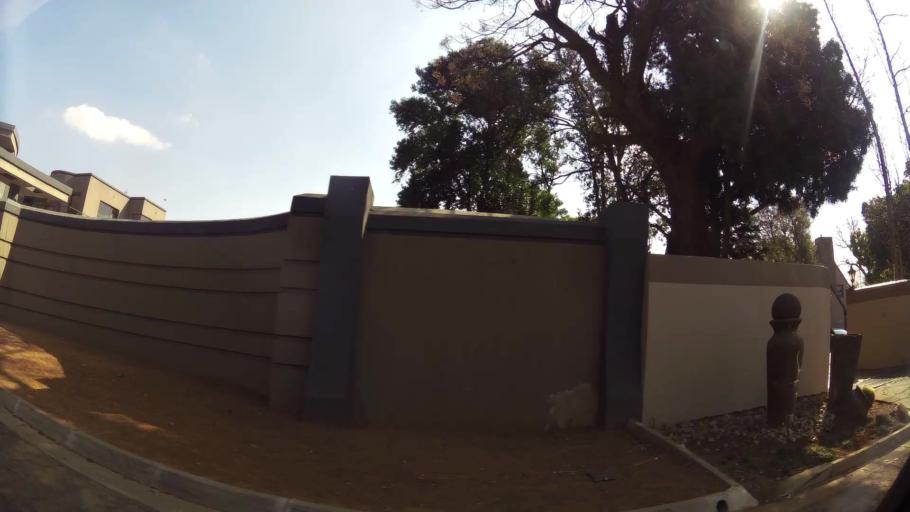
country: ZA
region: Gauteng
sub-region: Ekurhuleni Metropolitan Municipality
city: Benoni
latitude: -26.1825
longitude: 28.2930
